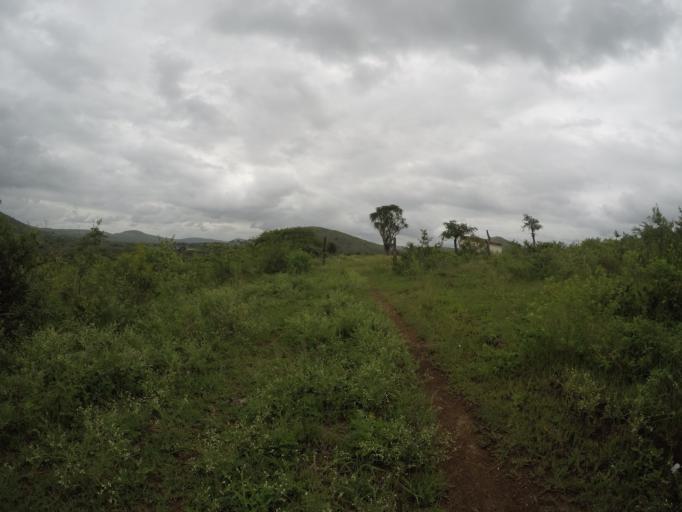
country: ZA
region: KwaZulu-Natal
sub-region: uThungulu District Municipality
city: Empangeni
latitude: -28.5874
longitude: 31.8669
